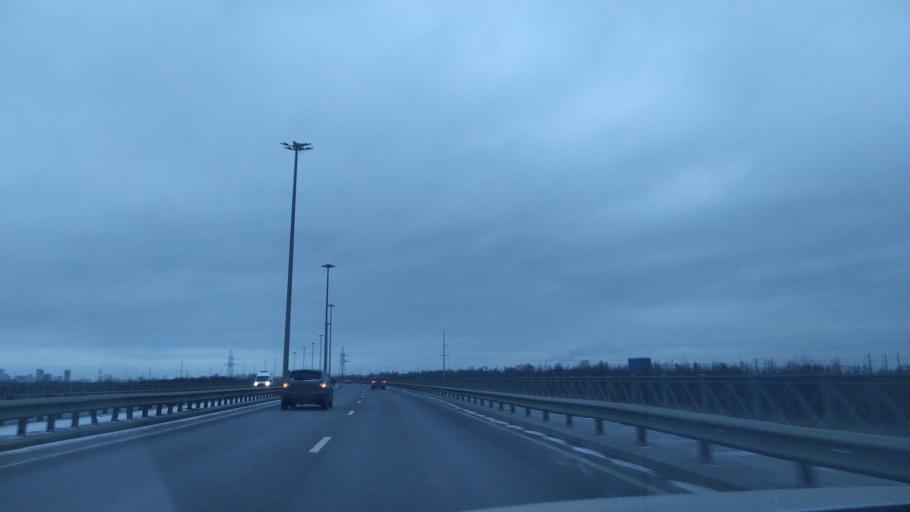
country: RU
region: St.-Petersburg
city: Shushary
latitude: 59.7691
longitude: 30.4008
